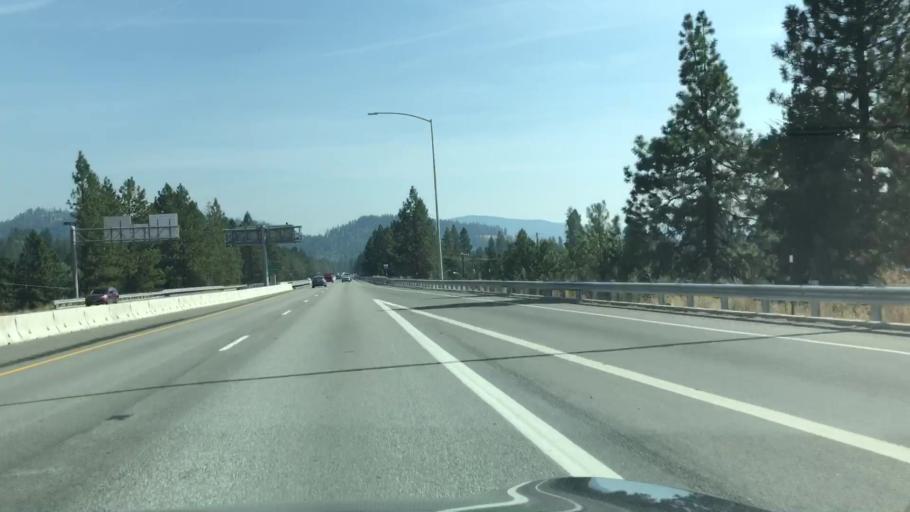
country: US
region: Idaho
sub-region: Kootenai County
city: Coeur d'Alene
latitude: 47.6846
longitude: -116.7609
